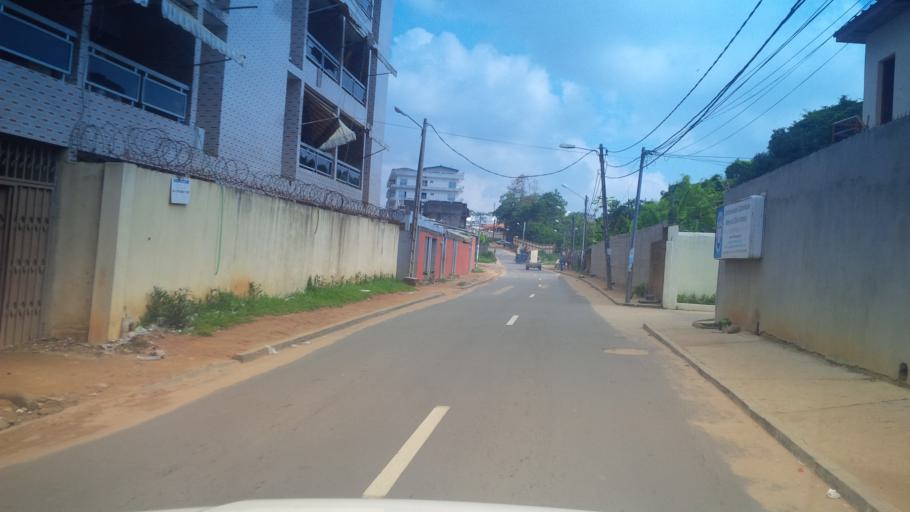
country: CI
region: Lagunes
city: Abobo
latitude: 5.3804
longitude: -3.9539
